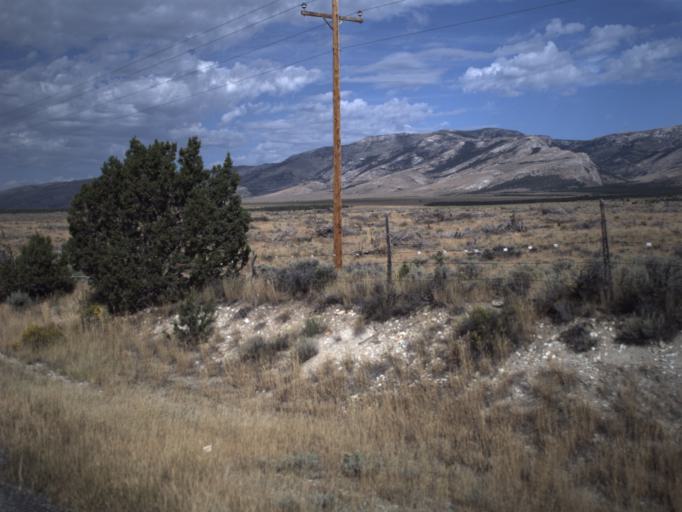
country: US
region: Idaho
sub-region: Cassia County
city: Burley
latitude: 41.8164
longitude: -113.3810
